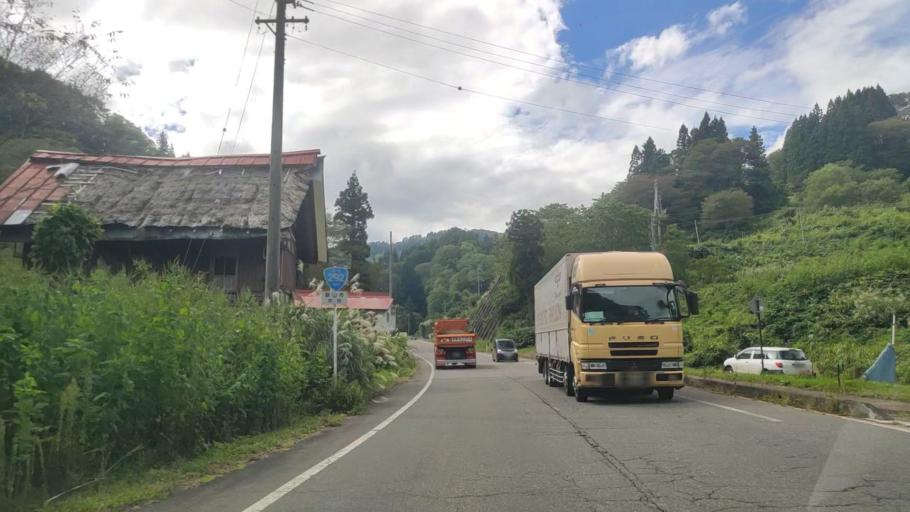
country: JP
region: Nagano
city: Iiyama
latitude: 36.9092
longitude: 138.3156
